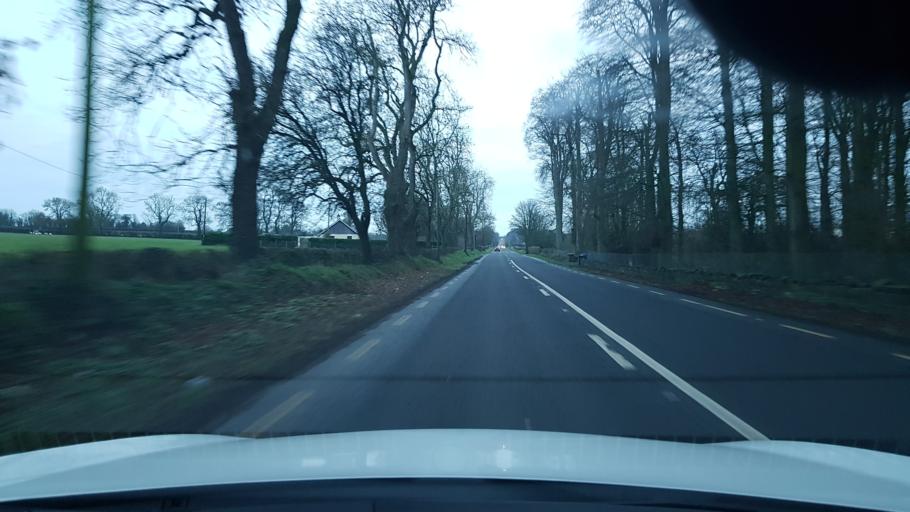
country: IE
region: Leinster
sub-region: An Mhi
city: Navan
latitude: 53.6223
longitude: -6.6473
